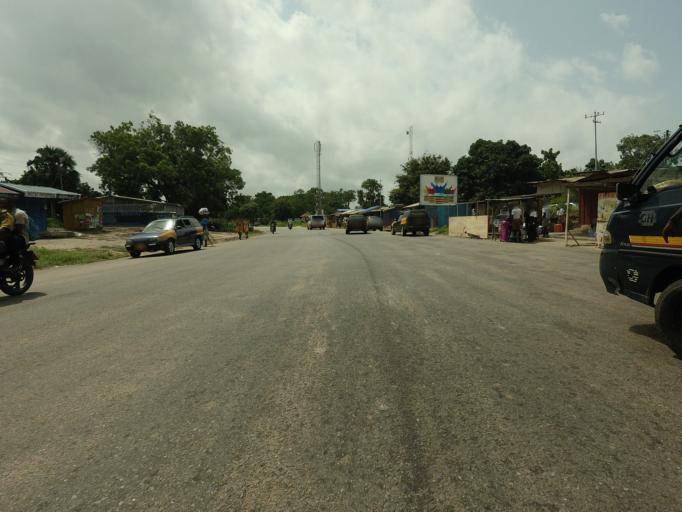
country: TG
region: Maritime
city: Lome
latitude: 6.1166
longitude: 1.1330
